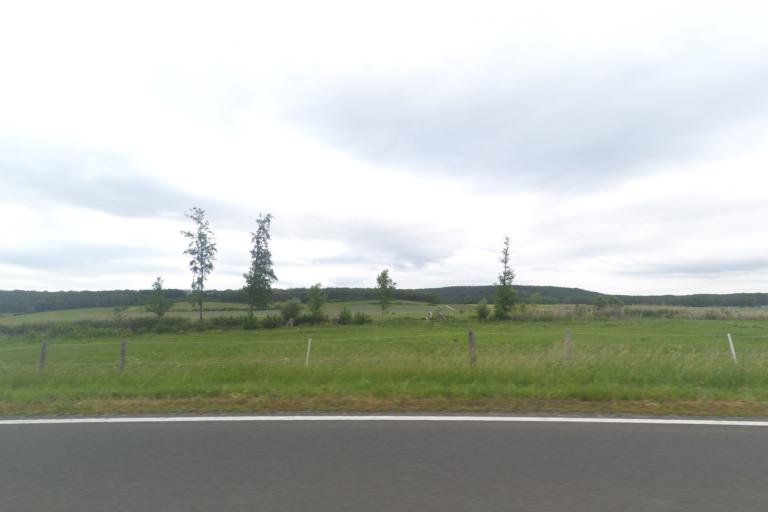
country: DE
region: Bavaria
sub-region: Regierungsbezirk Mittelfranken
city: Sugenheim
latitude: 49.6163
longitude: 10.4640
